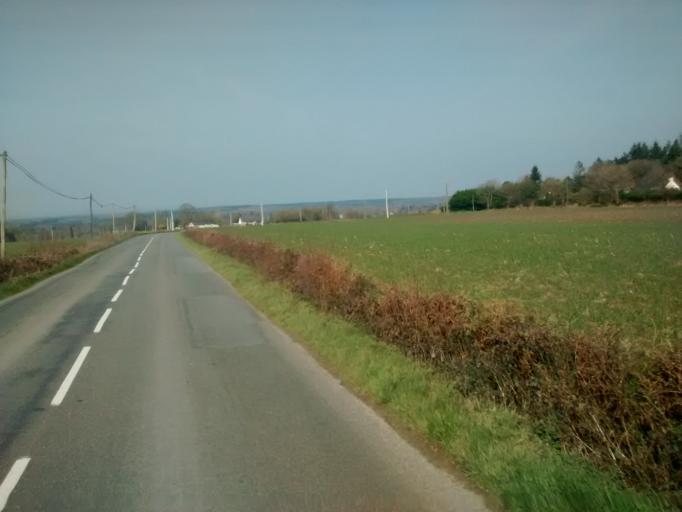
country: FR
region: Brittany
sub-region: Departement d'Ille-et-Vilaine
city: Paimpont
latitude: 48.0412
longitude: -2.1832
